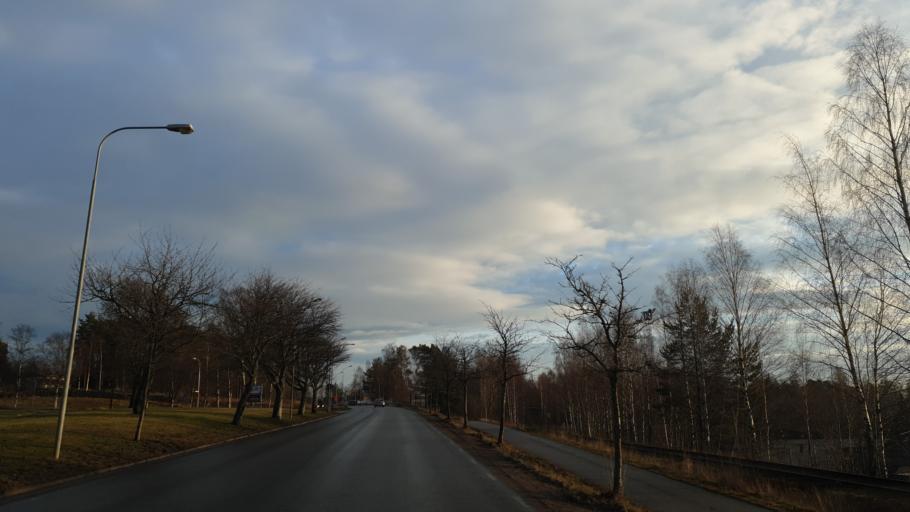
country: SE
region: Gaevleborg
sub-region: Hudiksvalls Kommun
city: Hudiksvall
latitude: 61.7243
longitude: 17.1388
